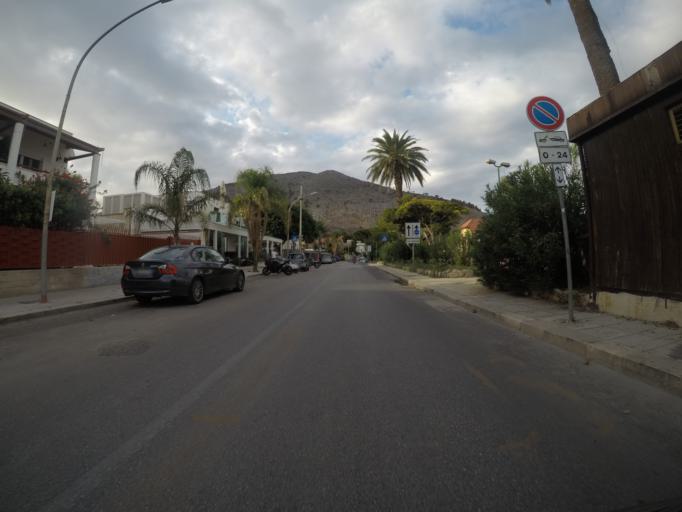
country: IT
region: Sicily
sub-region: Palermo
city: Palermo
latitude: 38.2031
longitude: 13.3258
